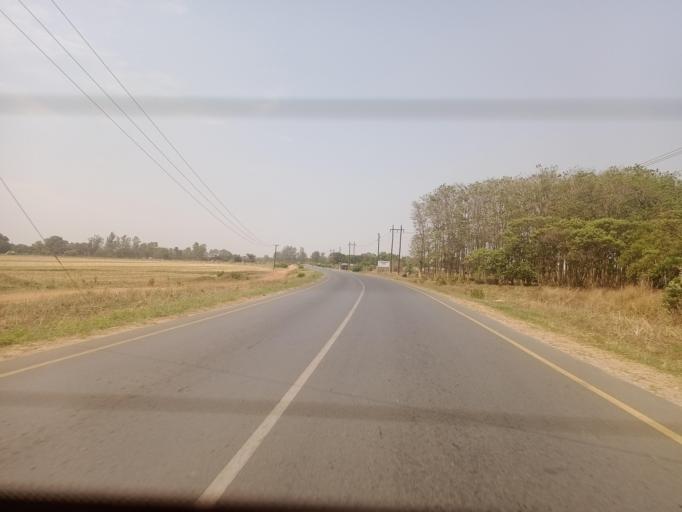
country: ZM
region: Lusaka
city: Lusaka
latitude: -15.2728
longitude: 28.4071
